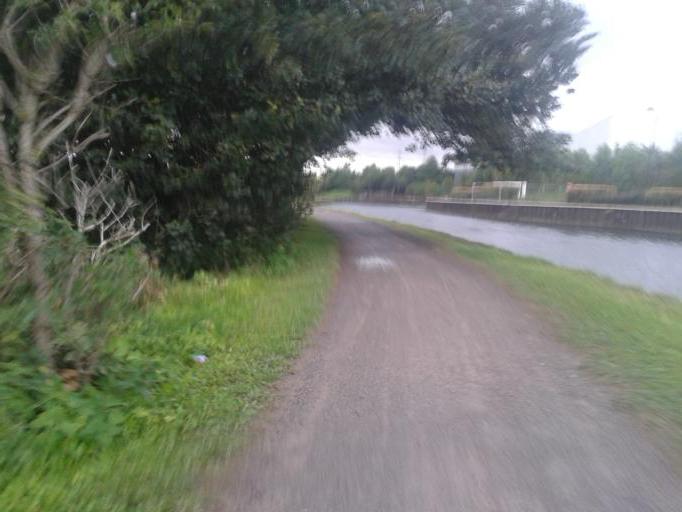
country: GB
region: England
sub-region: Essex
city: Waltham Abbey
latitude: 51.6557
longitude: -0.0201
